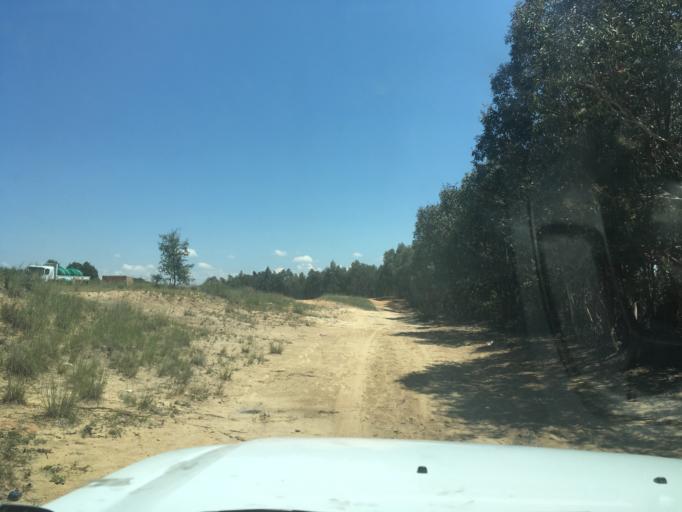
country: LS
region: Butha-Buthe
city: Butha-Buthe
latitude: -28.7252
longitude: 28.3618
